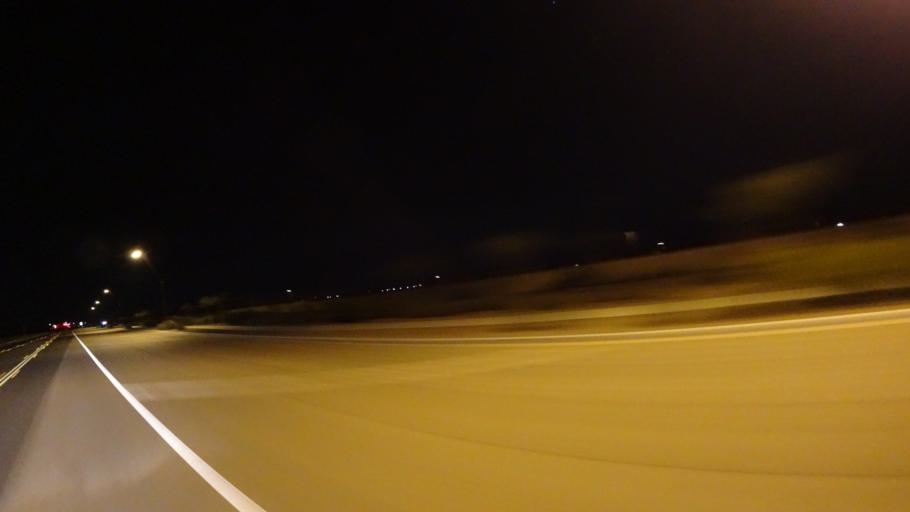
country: US
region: Arizona
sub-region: Maricopa County
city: Queen Creek
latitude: 33.2485
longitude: -111.6971
